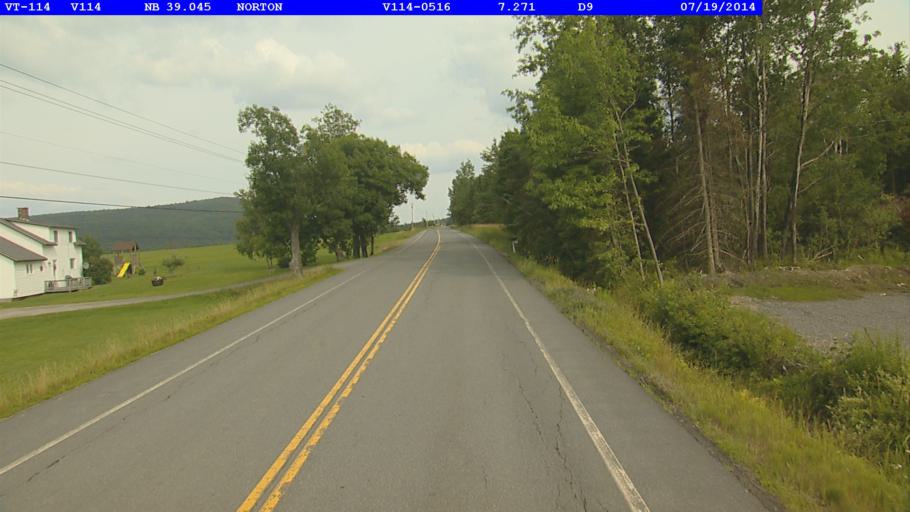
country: CA
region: Quebec
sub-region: Estrie
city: Coaticook
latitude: 45.0021
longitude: -71.7588
